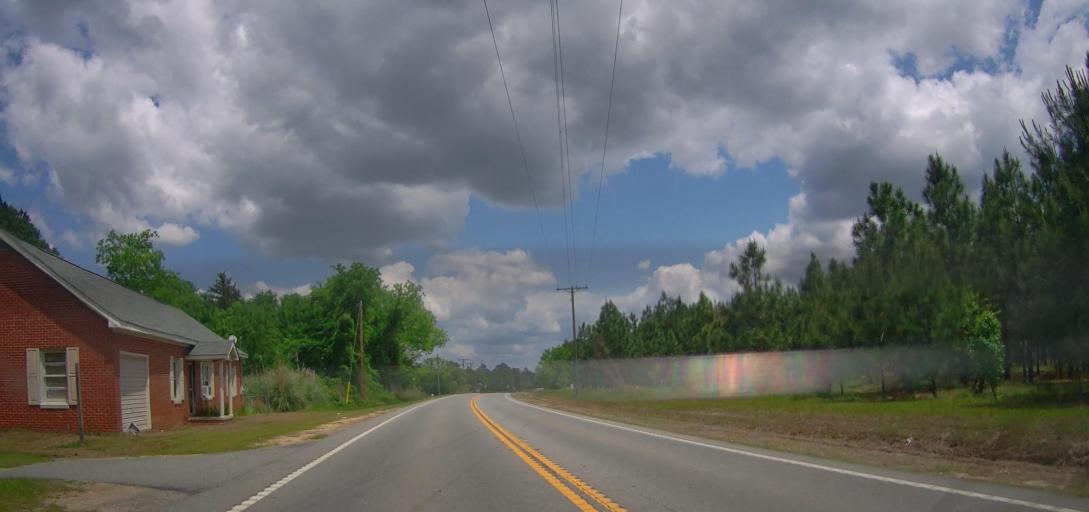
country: US
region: Georgia
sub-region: Laurens County
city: East Dublin
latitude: 32.5674
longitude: -82.8034
